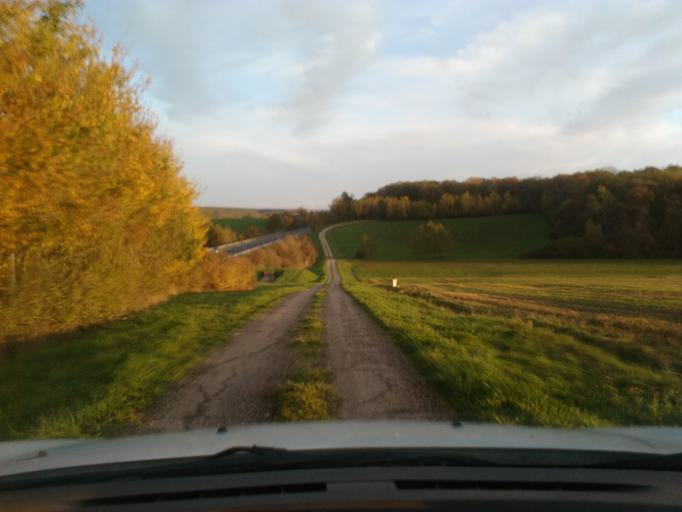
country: FR
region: Lorraine
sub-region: Departement des Vosges
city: Mirecourt
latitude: 48.2519
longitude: 6.1764
